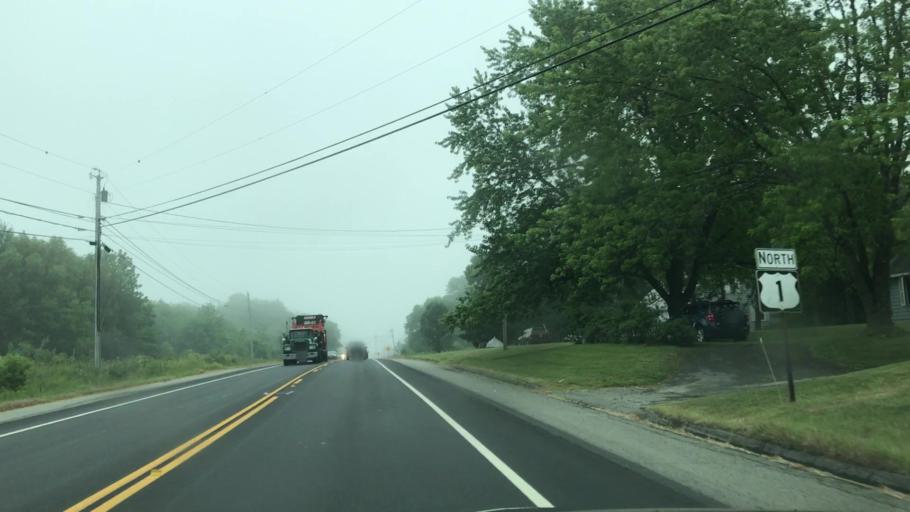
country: US
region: Maine
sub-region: Lincoln County
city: Waldoboro
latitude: 44.1126
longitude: -69.3146
